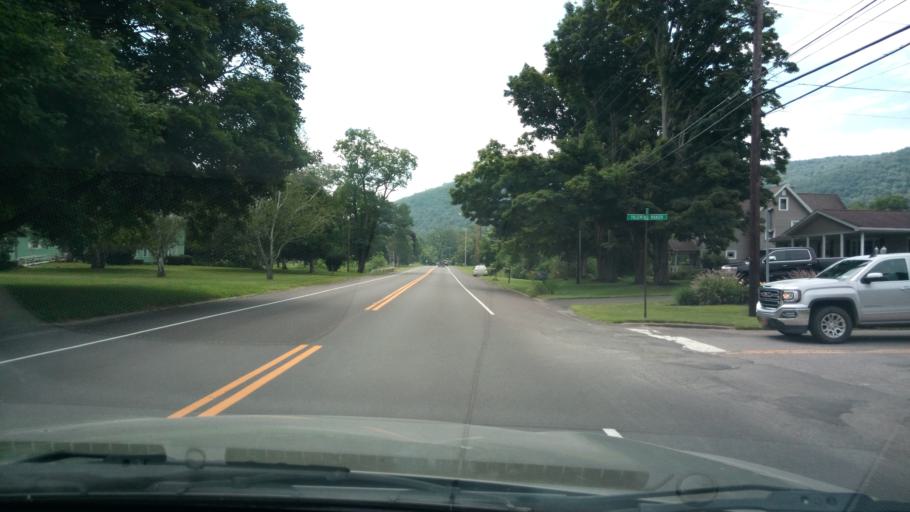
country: US
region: New York
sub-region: Chemung County
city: Southport
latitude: 42.0556
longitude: -76.7814
